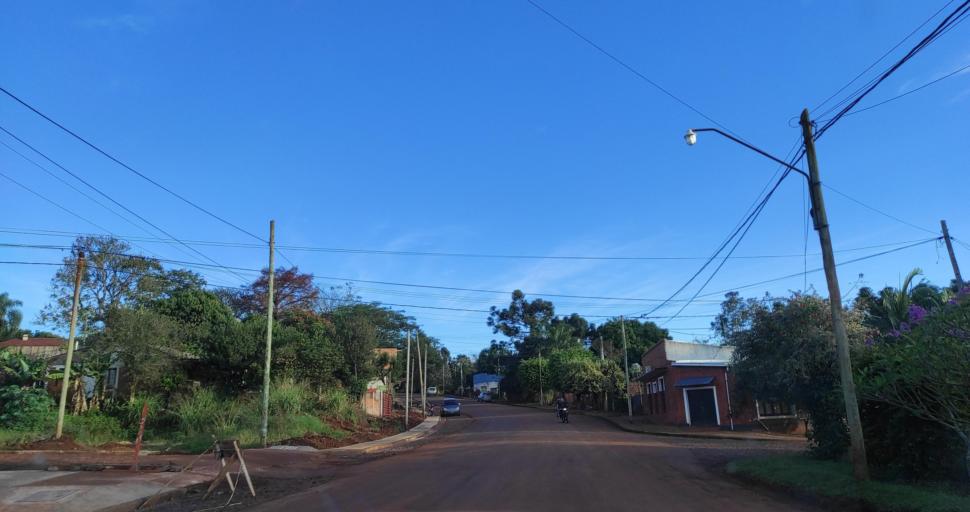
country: AR
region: Misiones
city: Puerto Rico
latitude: -26.7969
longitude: -55.0200
